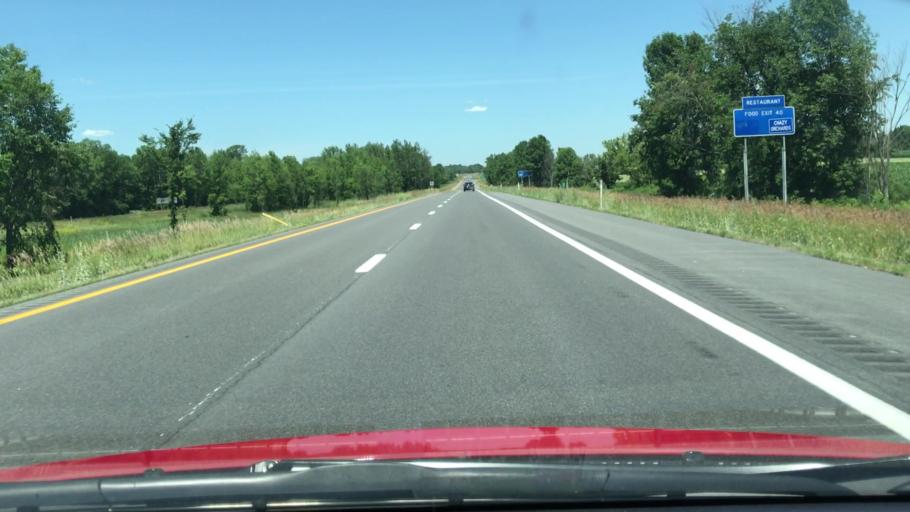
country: US
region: New York
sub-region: Clinton County
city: Cumberland Head
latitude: 44.7714
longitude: -73.4338
